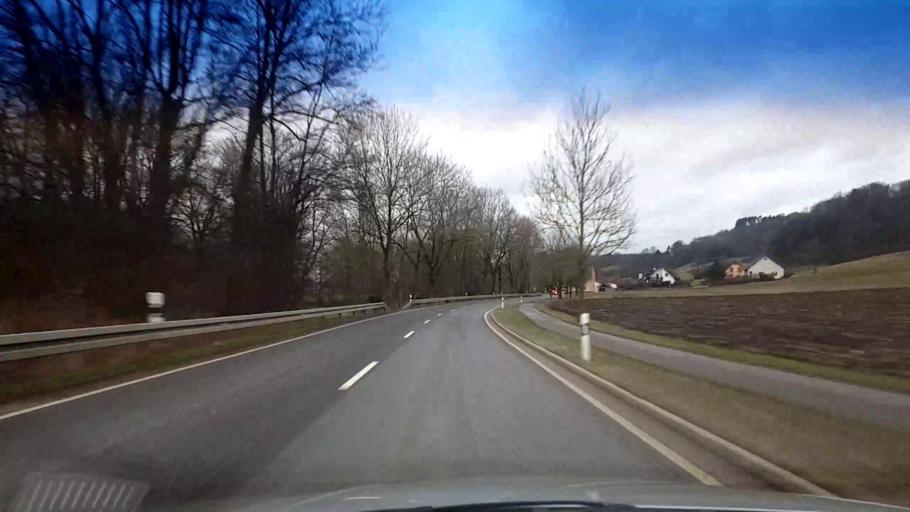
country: DE
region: Bavaria
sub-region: Upper Franconia
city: Wattendorf
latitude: 50.0666
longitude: 11.0686
